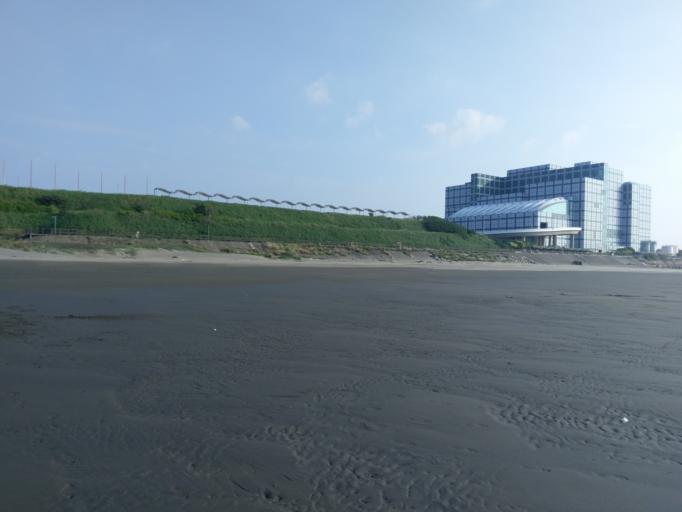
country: TW
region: Taiwan
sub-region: Hsinchu
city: Hsinchu
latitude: 24.8379
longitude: 120.9168
